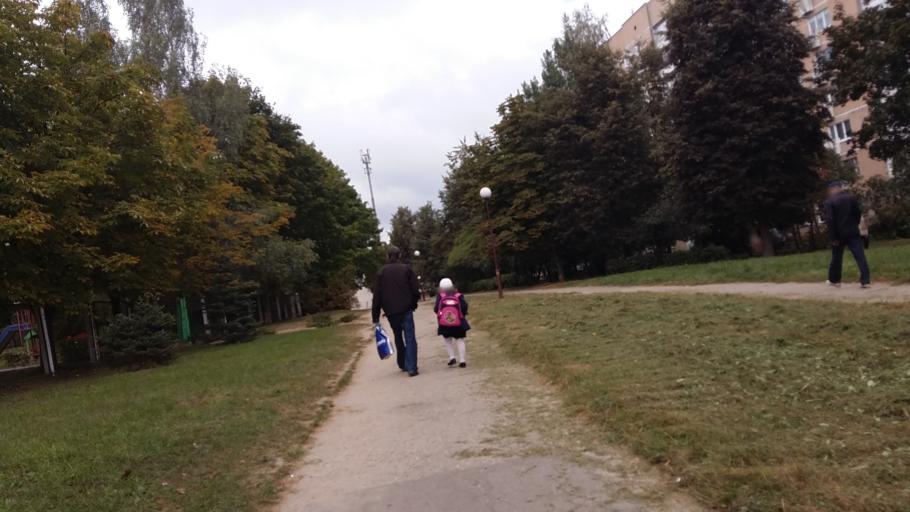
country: BY
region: Grodnenskaya
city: Hrodna
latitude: 53.6952
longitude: 23.8056
